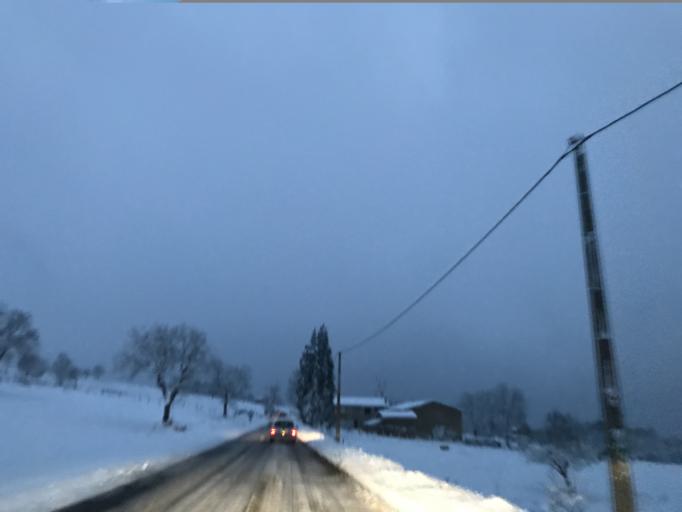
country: FR
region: Auvergne
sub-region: Departement du Puy-de-Dome
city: Courpiere
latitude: 45.7173
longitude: 3.5906
